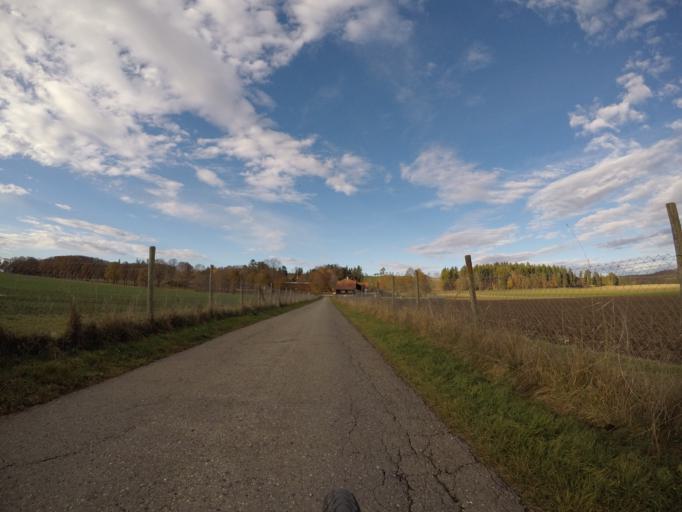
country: DE
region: Baden-Wuerttemberg
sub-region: Tuebingen Region
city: Sankt Johann
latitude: 48.4718
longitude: 9.3059
